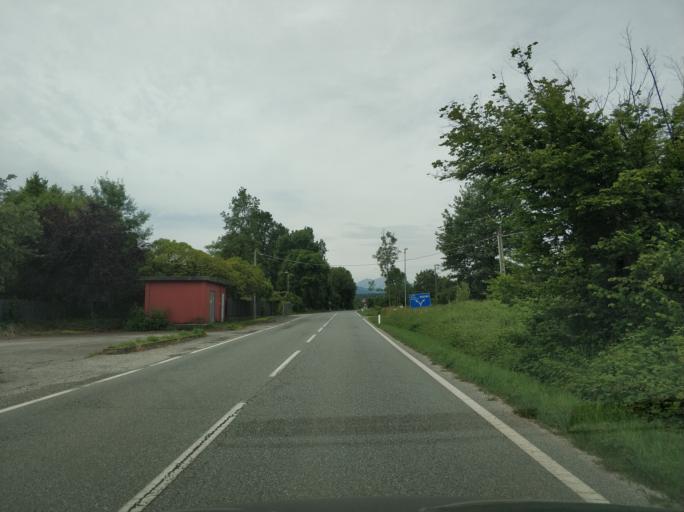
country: IT
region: Piedmont
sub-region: Provincia di Torino
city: Levone
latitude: 45.3188
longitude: 7.6173
